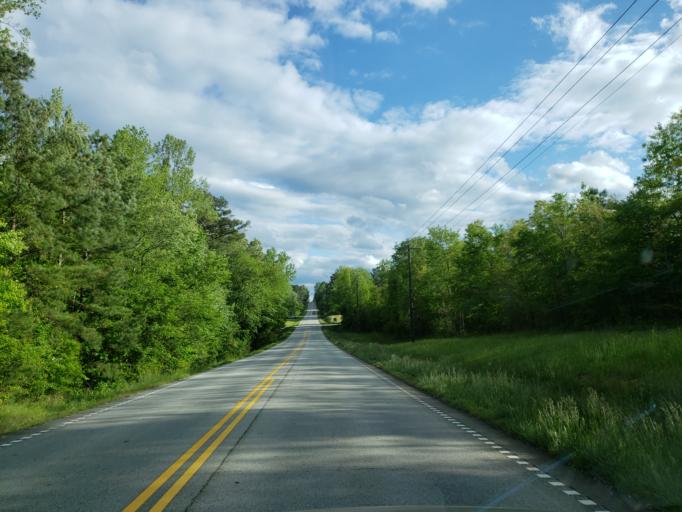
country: US
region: Georgia
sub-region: Haralson County
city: Tallapoosa
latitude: 33.8191
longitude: -85.2919
